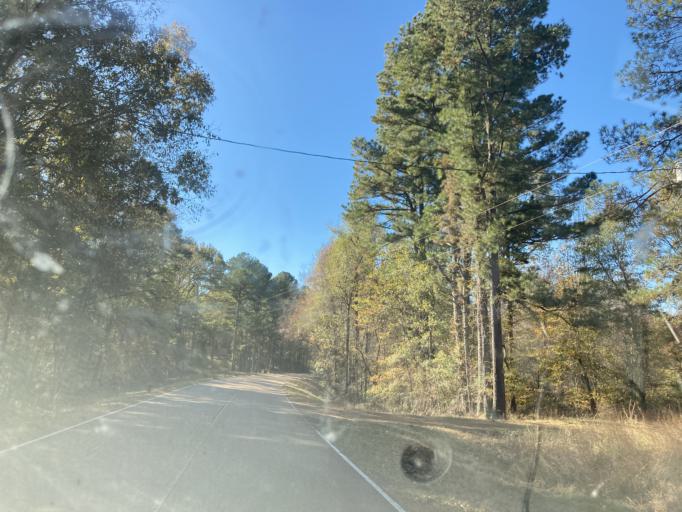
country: US
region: Mississippi
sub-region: Hinds County
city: Lynchburg
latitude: 32.6246
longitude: -90.5221
